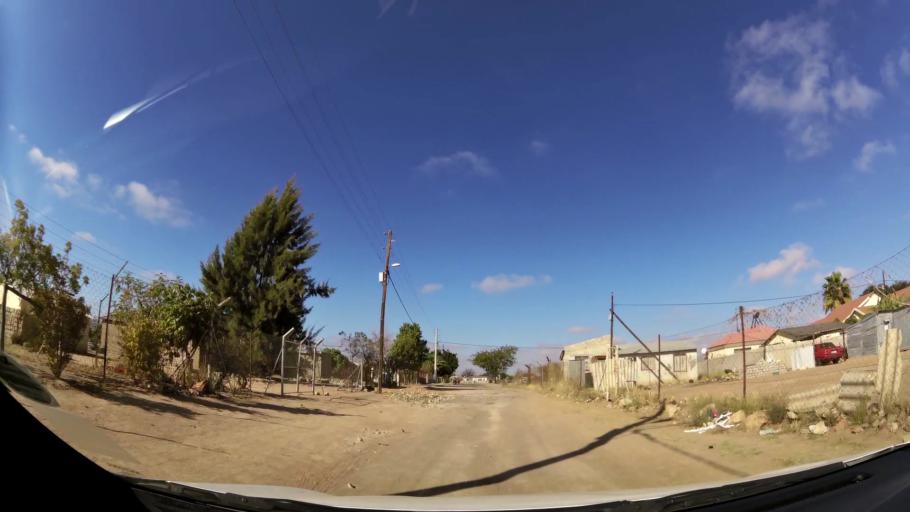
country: ZA
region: Limpopo
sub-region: Capricorn District Municipality
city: Polokwane
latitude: -23.8482
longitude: 29.4054
